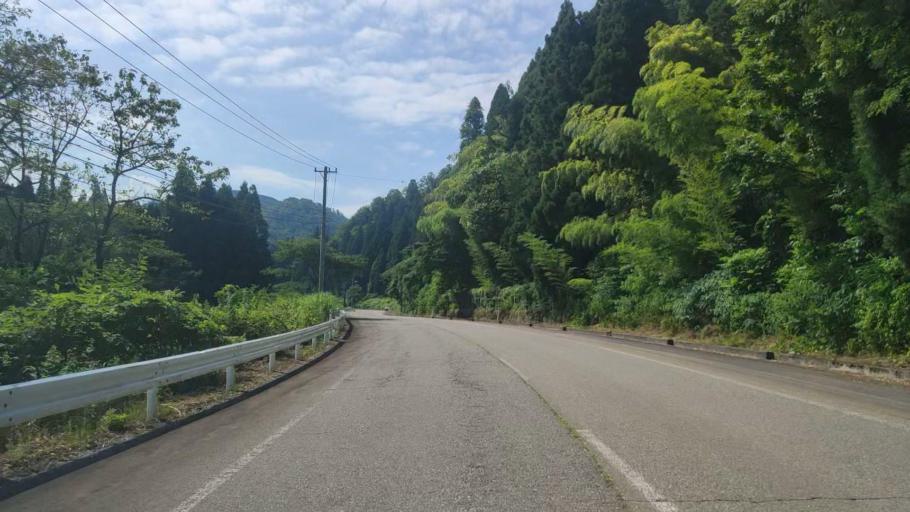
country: JP
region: Ishikawa
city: Komatsu
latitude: 36.3253
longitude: 136.5291
